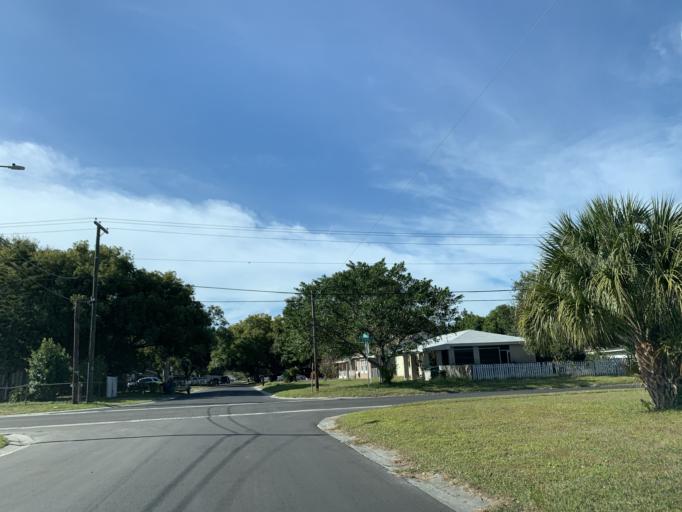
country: US
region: Florida
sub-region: Hillsborough County
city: Tampa
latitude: 27.8854
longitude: -82.5100
